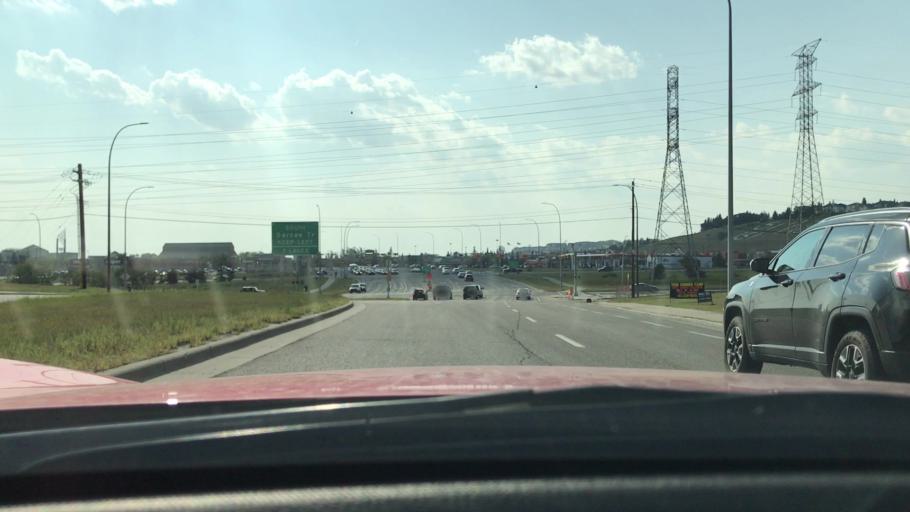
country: CA
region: Alberta
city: Calgary
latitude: 51.0179
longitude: -114.1624
